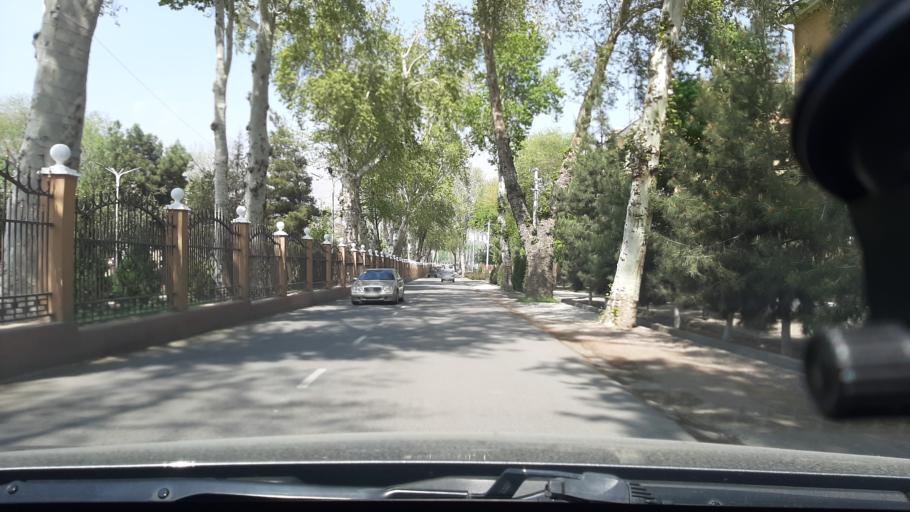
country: TJ
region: Viloyati Sughd
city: Khujand
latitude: 40.2854
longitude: 69.6191
